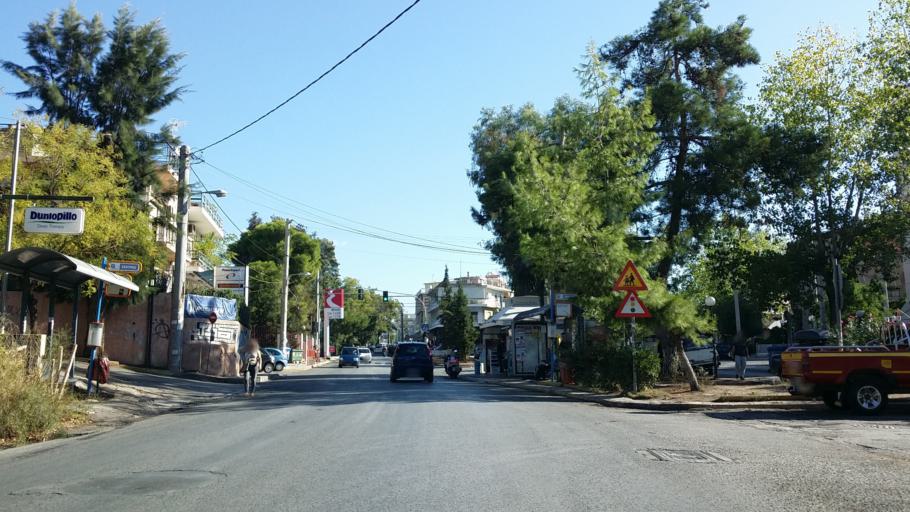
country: GR
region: Attica
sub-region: Nomarchia Athinas
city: Irakleio
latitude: 38.0484
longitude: 23.7614
